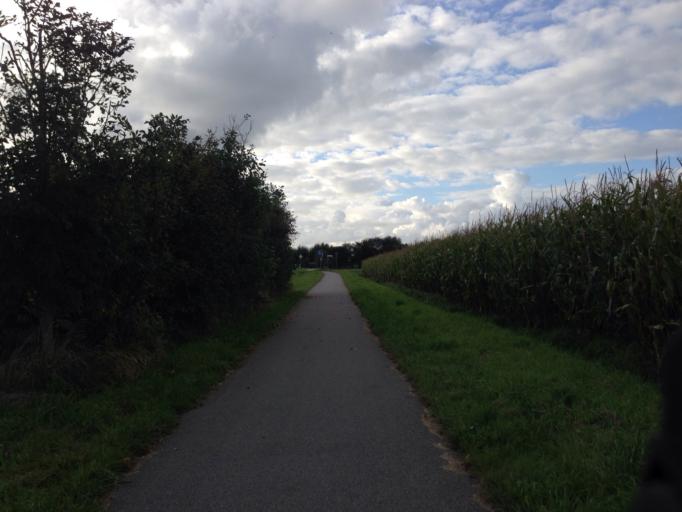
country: DE
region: Schleswig-Holstein
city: Oldsum
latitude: 54.7287
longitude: 8.4483
